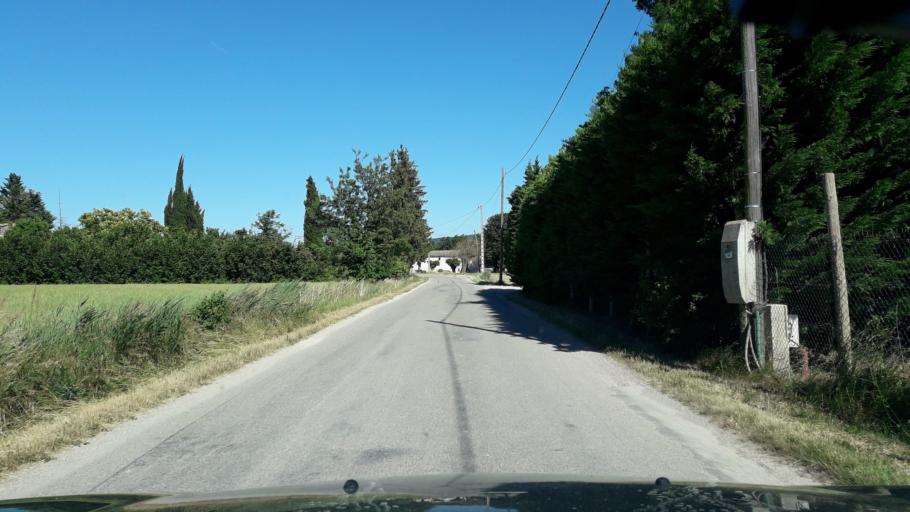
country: FR
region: Rhone-Alpes
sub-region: Departement de l'Ardeche
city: Le Pouzin
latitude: 44.7514
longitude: 4.7752
